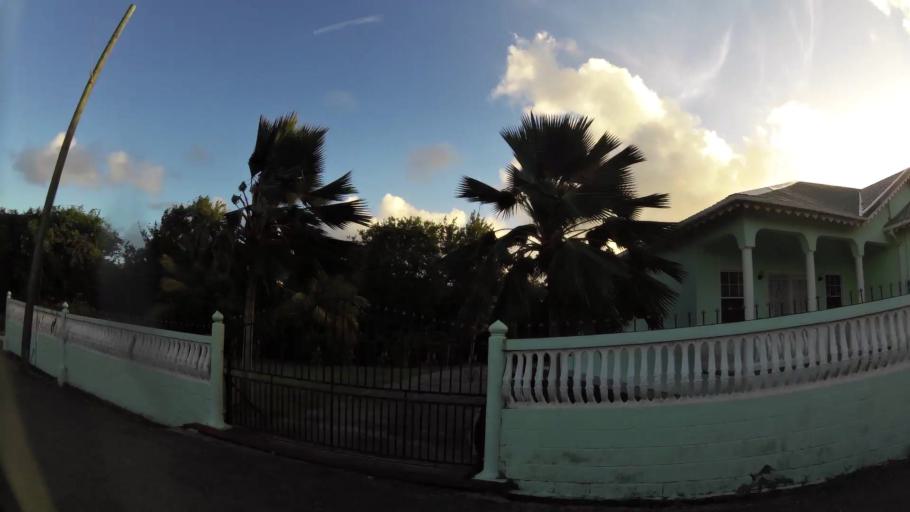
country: LC
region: Gros-Islet
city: Gros Islet
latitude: 14.0706
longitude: -60.9363
